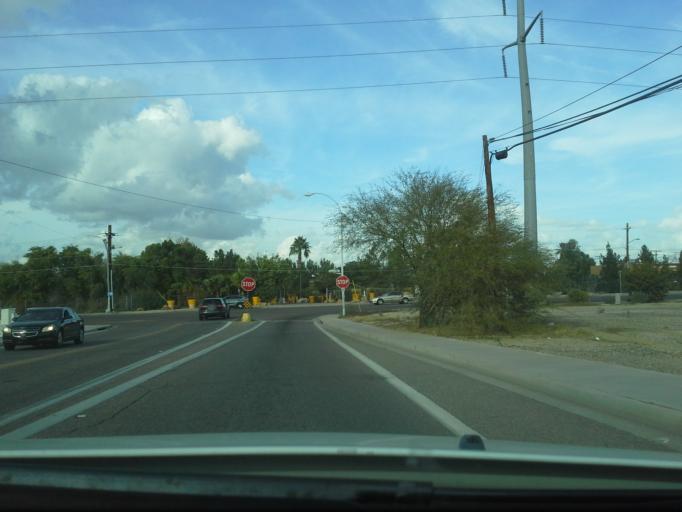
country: US
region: Arizona
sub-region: Maricopa County
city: Phoenix
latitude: 33.3771
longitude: -112.0833
